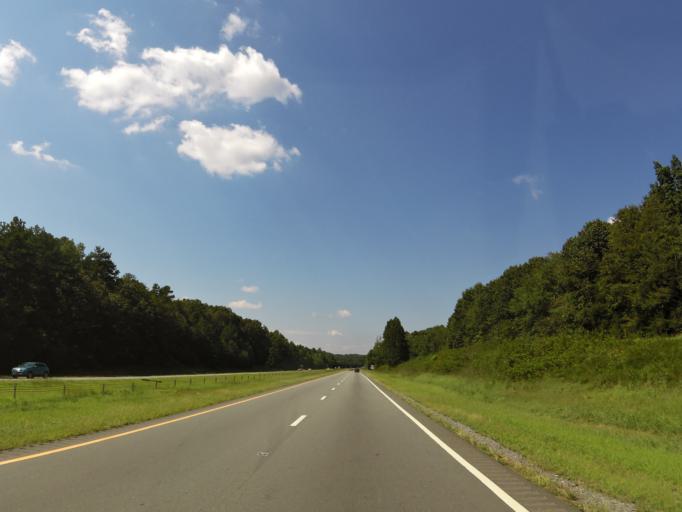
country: US
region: North Carolina
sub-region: Gaston County
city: Dallas
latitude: 35.3854
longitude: -81.2043
